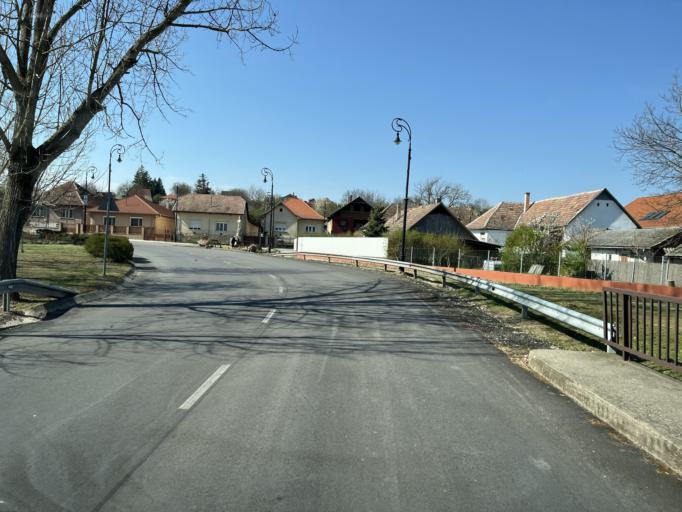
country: HU
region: Pest
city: Orbottyan
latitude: 47.7378
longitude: 19.2904
